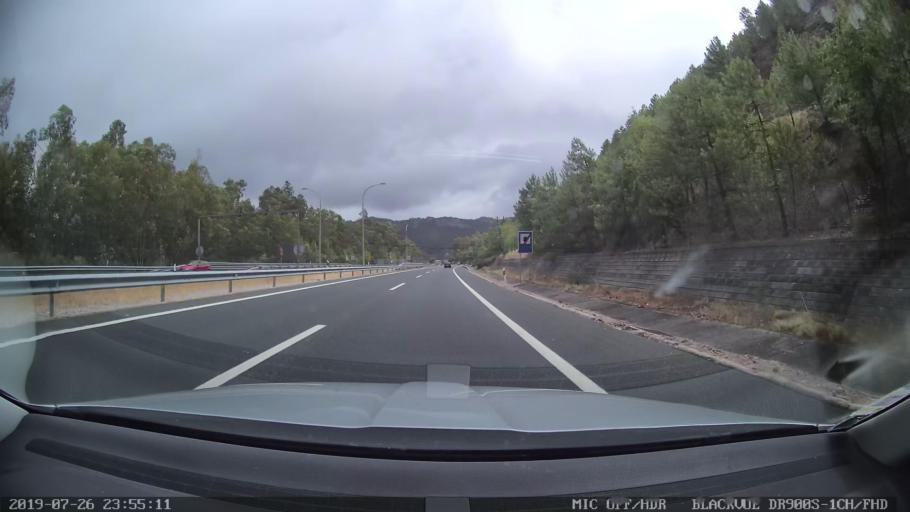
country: ES
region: Extremadura
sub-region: Provincia de Caceres
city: Higuera
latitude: 39.6973
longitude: -5.6952
